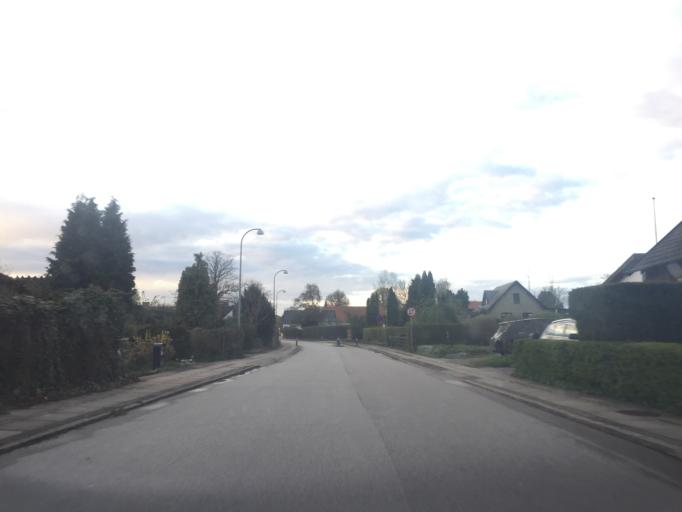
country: DK
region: Capital Region
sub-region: Rodovre Kommune
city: Rodovre
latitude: 55.6549
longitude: 12.4438
